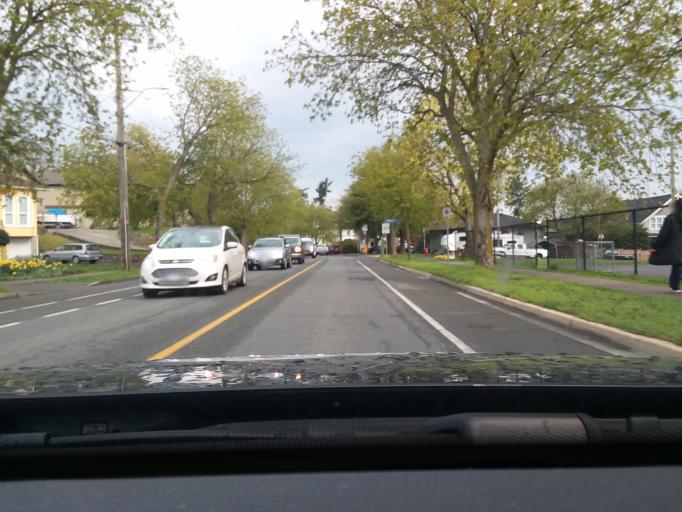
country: CA
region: British Columbia
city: Victoria
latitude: 48.4377
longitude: -123.3892
